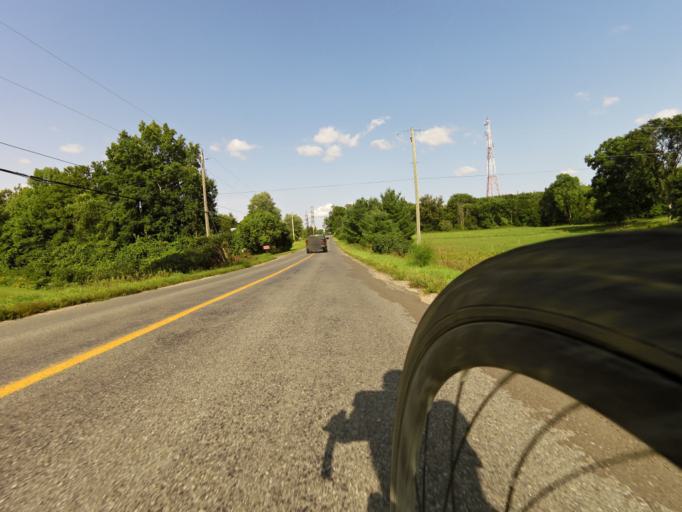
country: CA
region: Ontario
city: Kingston
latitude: 44.3630
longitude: -76.6303
